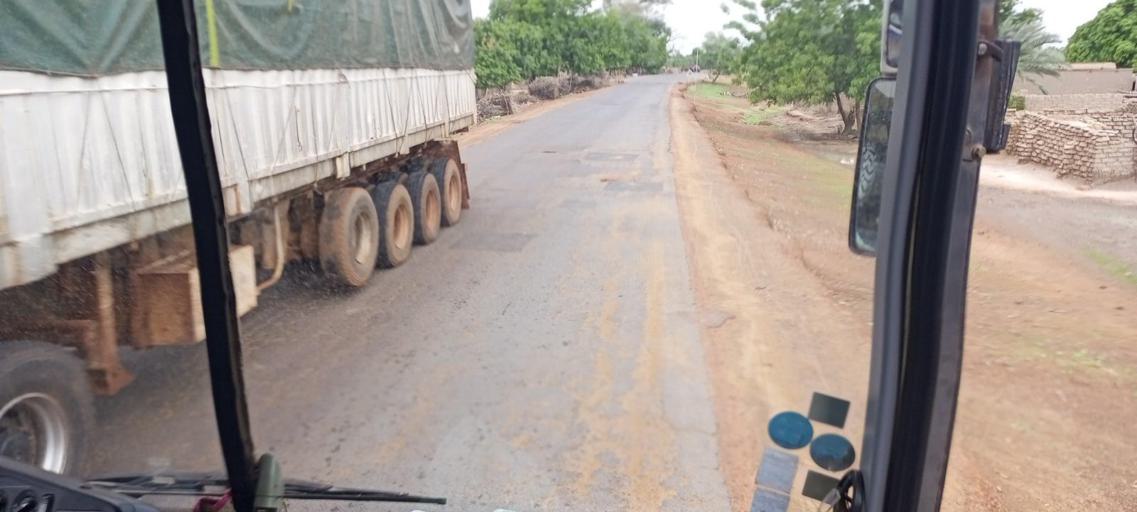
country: ML
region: Segou
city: Bla
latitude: 12.7365
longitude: -5.7266
